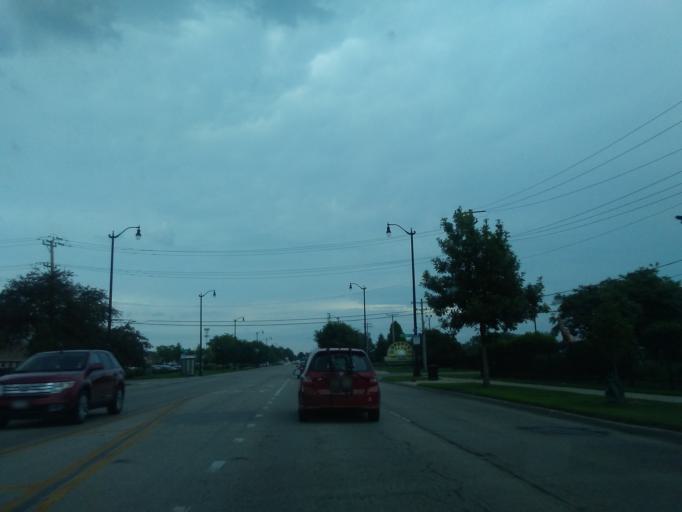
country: US
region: Illinois
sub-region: Cook County
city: Skokie
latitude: 42.0264
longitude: -87.7165
